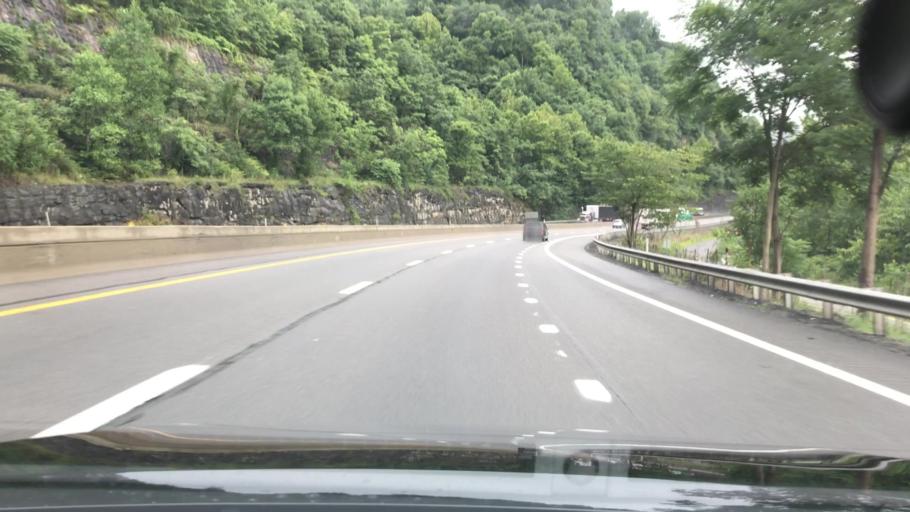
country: US
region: West Virginia
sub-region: Kanawha County
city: Montgomery
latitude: 38.0259
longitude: -81.3547
